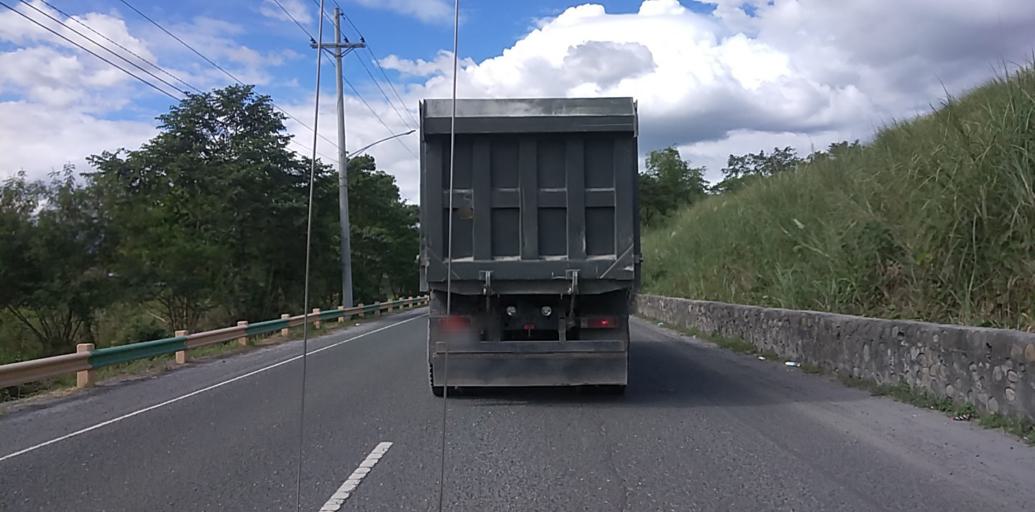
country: PH
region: Central Luzon
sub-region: Province of Pampanga
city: Dolores
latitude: 15.0904
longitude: 120.5363
